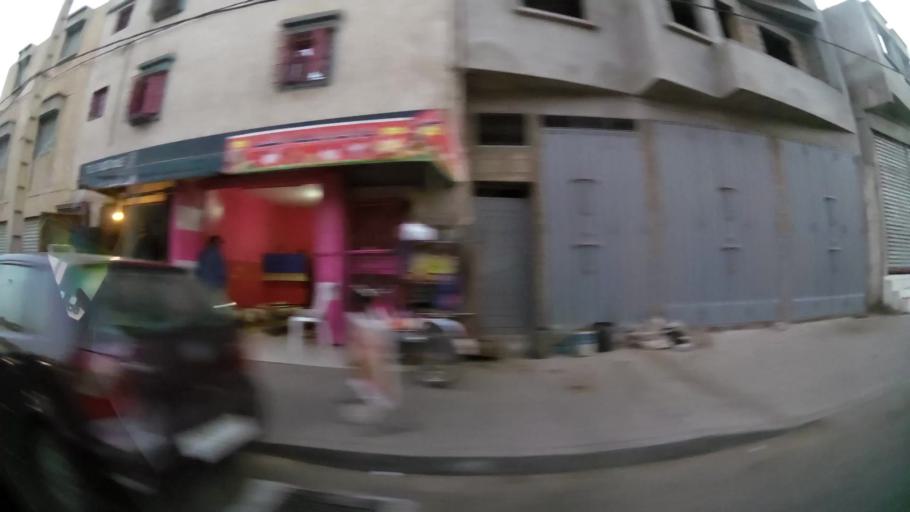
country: MA
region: Souss-Massa-Draa
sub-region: Inezgane-Ait Mellou
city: Inezgane
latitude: 30.3758
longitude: -9.4946
